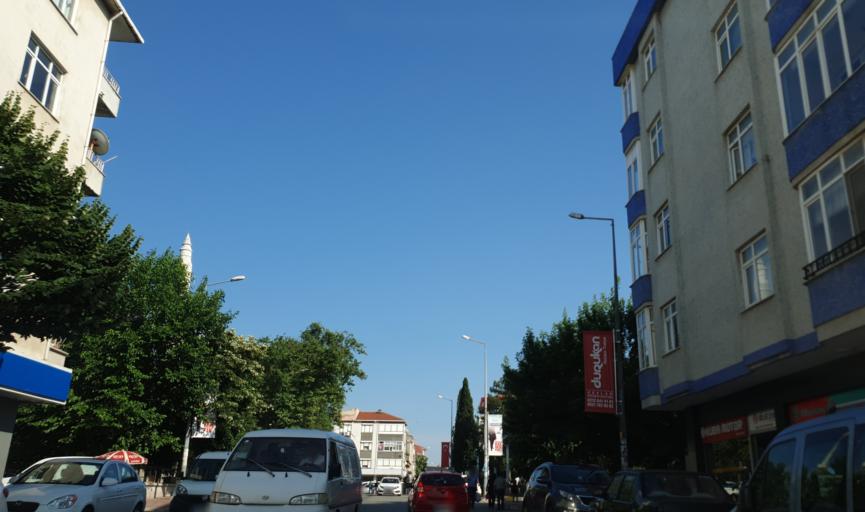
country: TR
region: Tekirdag
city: Saray
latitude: 41.4429
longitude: 27.9196
